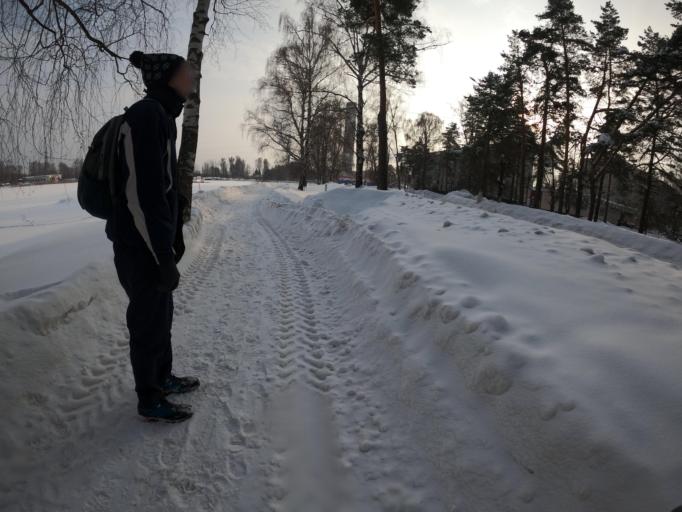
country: RU
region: Moskovskaya
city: Elektrogorsk
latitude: 55.8922
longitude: 38.7784
